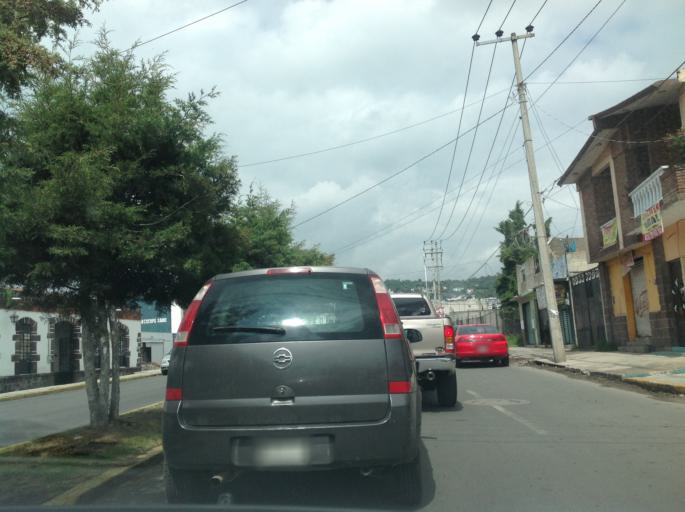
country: MX
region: Morelos
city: Tenango de Arista
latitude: 19.1054
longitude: -99.5857
